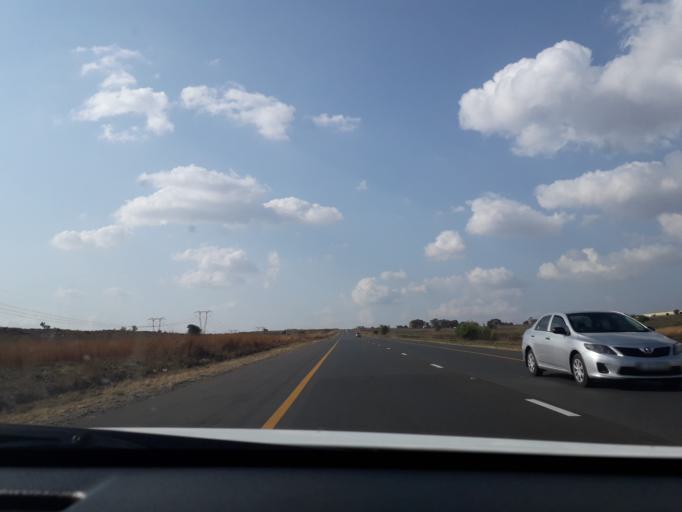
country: ZA
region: Gauteng
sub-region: City of Tshwane Metropolitan Municipality
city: Centurion
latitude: -25.9126
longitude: 28.2465
